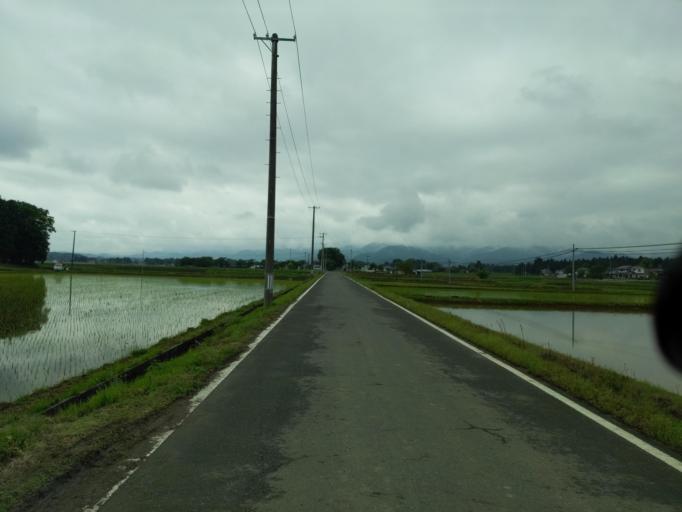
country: JP
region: Fukushima
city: Koriyama
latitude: 37.3534
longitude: 140.3055
